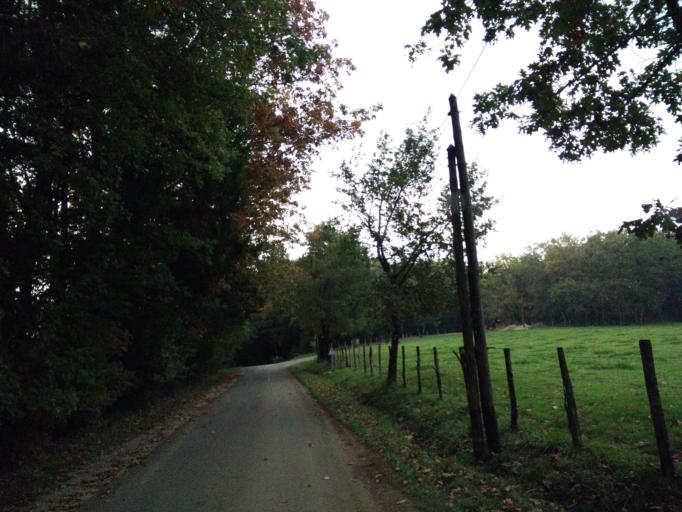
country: FR
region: Aquitaine
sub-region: Departement de la Dordogne
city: Rouffignac-Saint-Cernin-de-Reilhac
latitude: 45.0126
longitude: 0.9856
